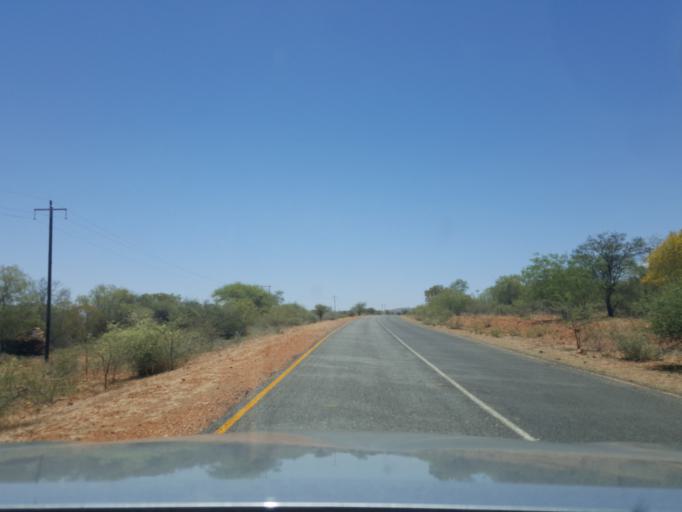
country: BW
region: South East
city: Ramotswa
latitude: -24.8973
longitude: 25.8845
